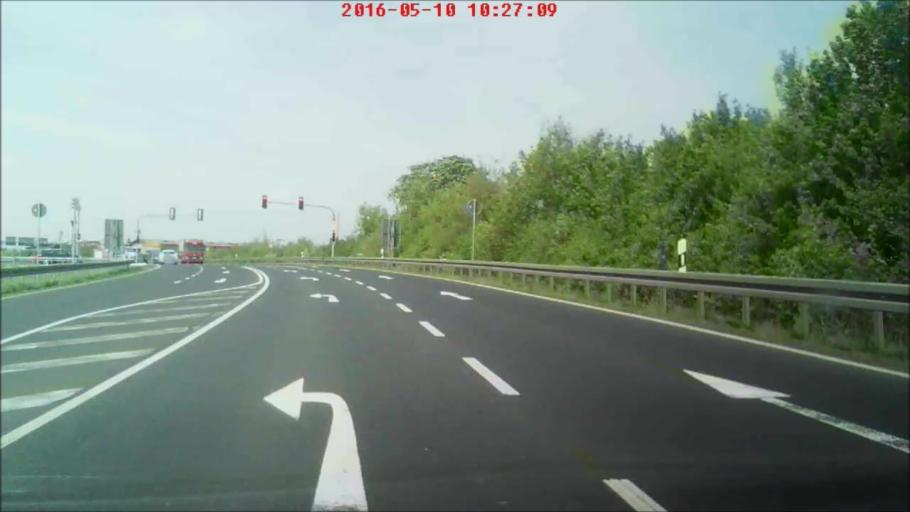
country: DE
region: Hesse
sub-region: Regierungsbezirk Kassel
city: Kunzell
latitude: 50.5539
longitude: 9.7357
